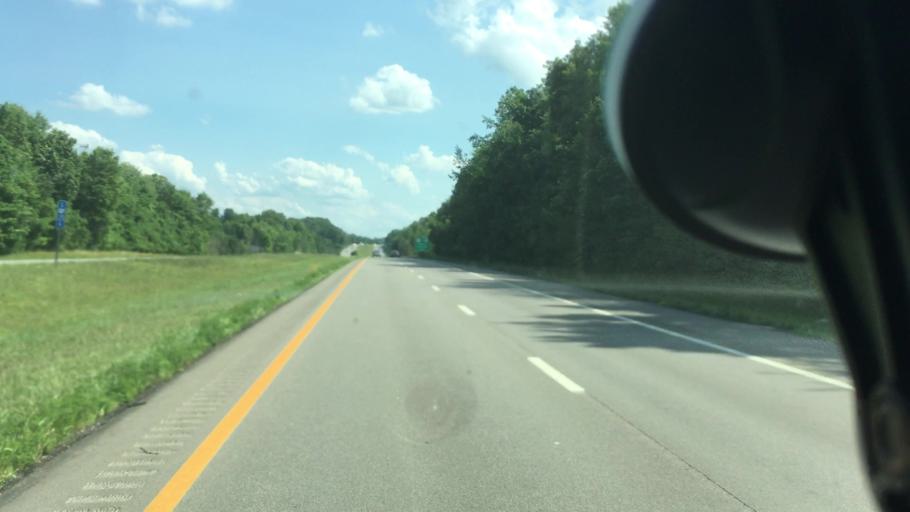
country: US
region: Ohio
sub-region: Mahoning County
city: Canfield
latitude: 41.0466
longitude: -80.7453
